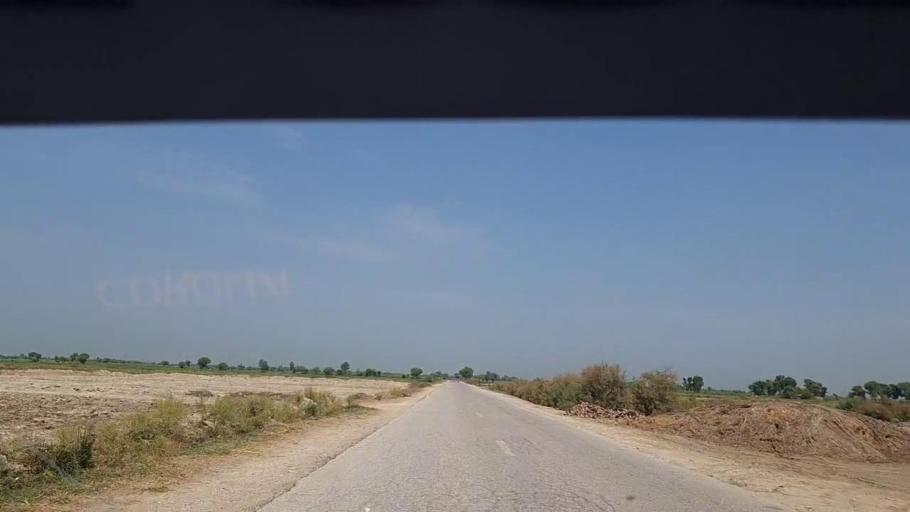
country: PK
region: Sindh
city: Thul
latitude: 28.1271
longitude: 68.8178
